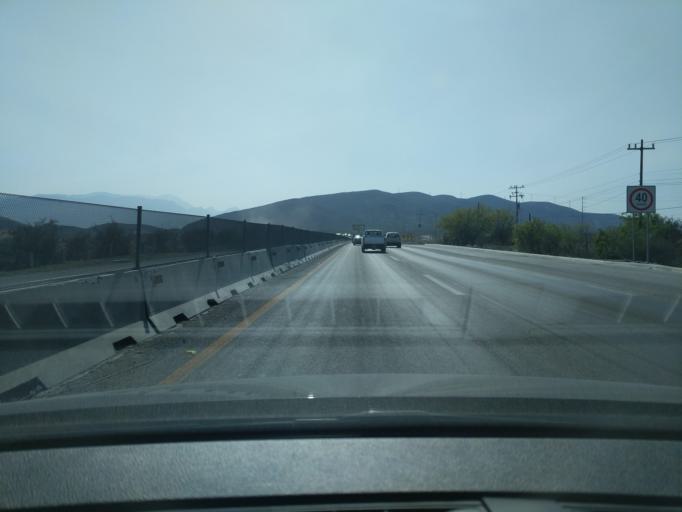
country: MX
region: Nuevo Leon
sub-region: Garcia
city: Los Parques
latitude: 25.7674
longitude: -100.4854
